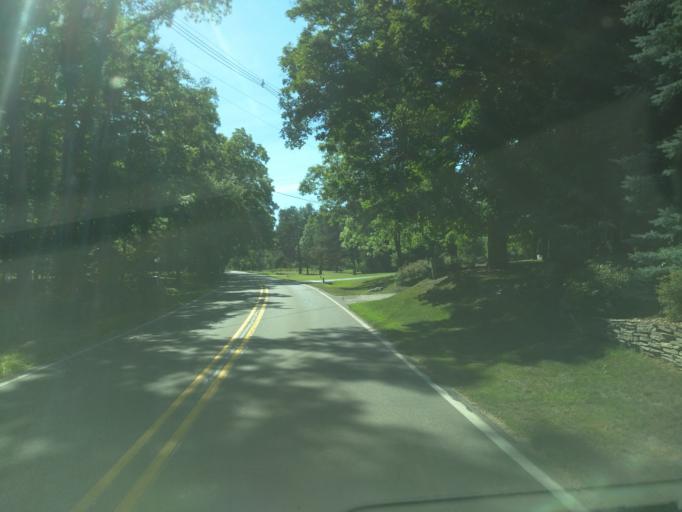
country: US
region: Michigan
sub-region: Eaton County
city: Waverly
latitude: 42.7654
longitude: -84.6220
